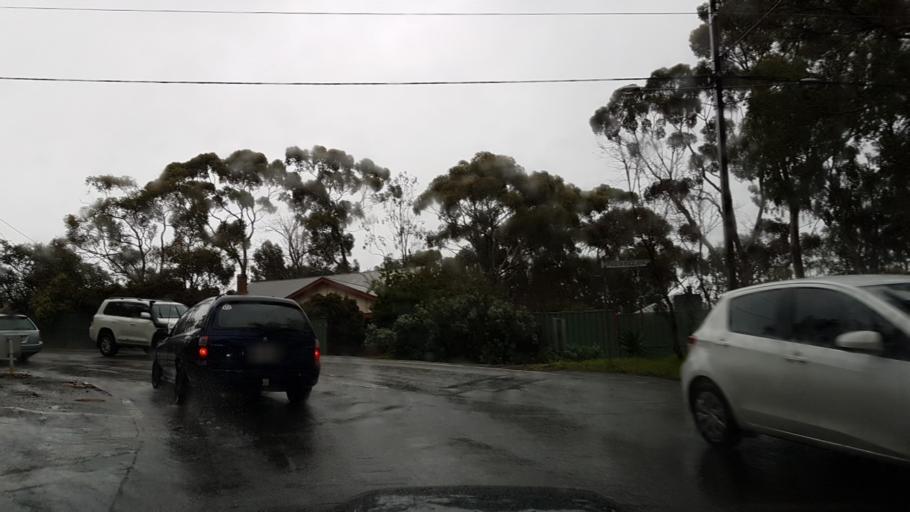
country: AU
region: South Australia
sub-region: Mitcham
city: Blackwood
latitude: -35.0240
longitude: 138.6221
